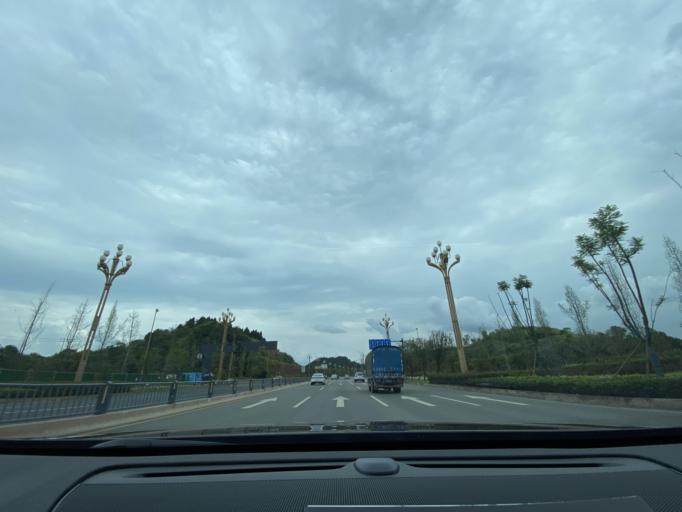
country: CN
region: Sichuan
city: Jiancheng
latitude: 30.4728
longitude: 104.4916
